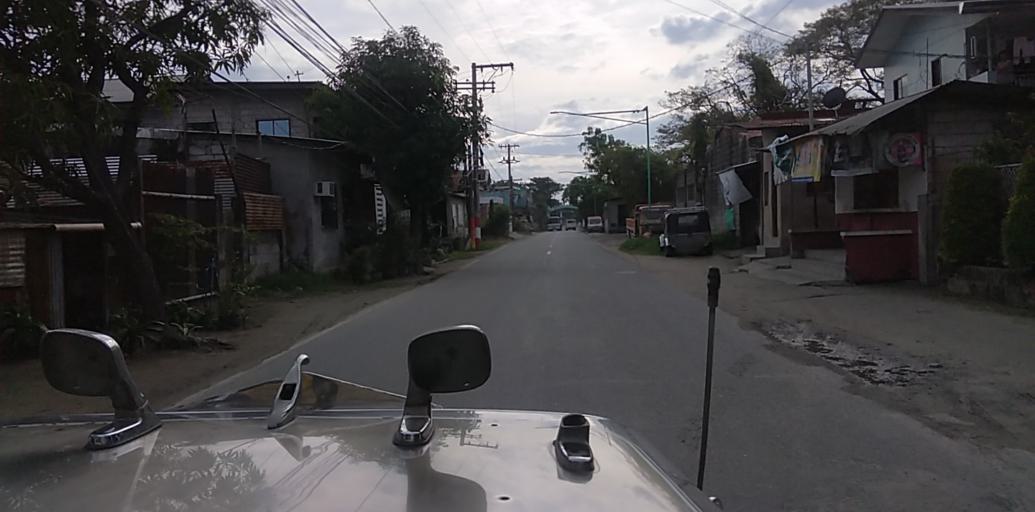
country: PH
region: Central Luzon
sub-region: Province of Pampanga
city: Minalin
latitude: 14.9844
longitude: 120.7018
